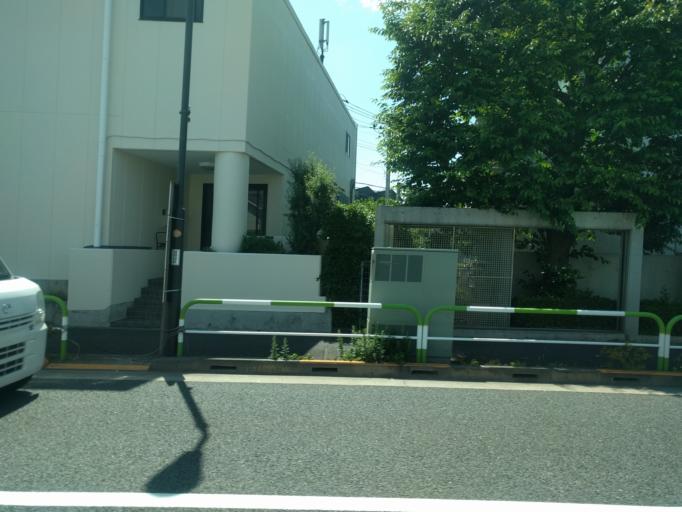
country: JP
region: Tokyo
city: Mitaka-shi
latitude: 35.6621
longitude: 139.6240
